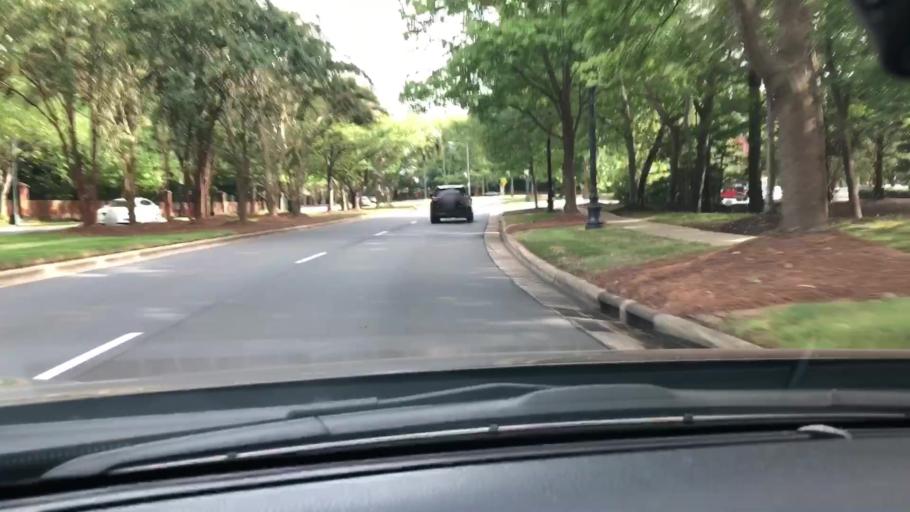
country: US
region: North Carolina
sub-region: Mecklenburg County
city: Charlotte
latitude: 35.1525
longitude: -80.8220
